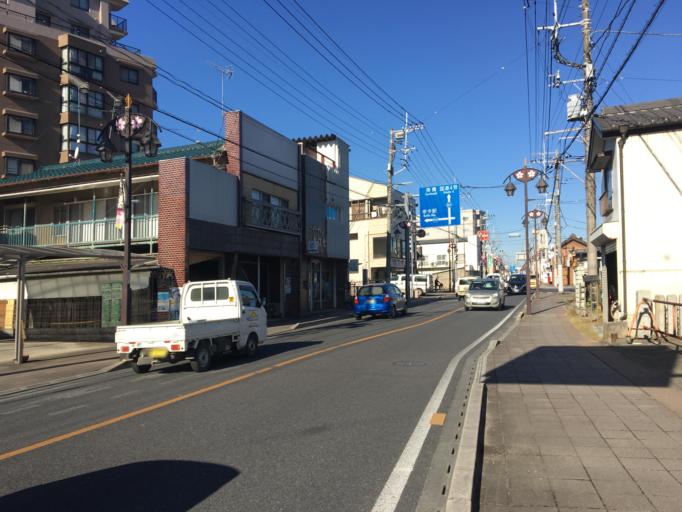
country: JP
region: Saitama
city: Satte
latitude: 36.0724
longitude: 139.7183
